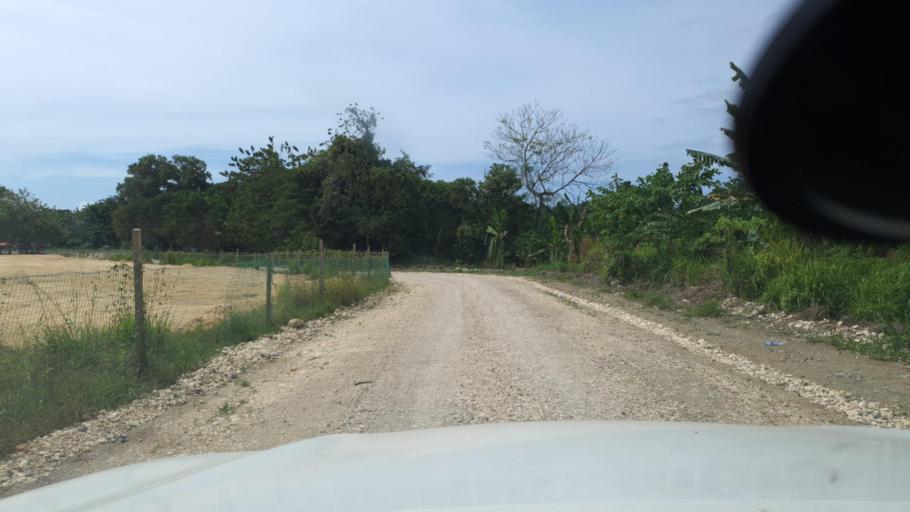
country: SB
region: Guadalcanal
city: Honiara
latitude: -9.4141
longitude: 159.8928
